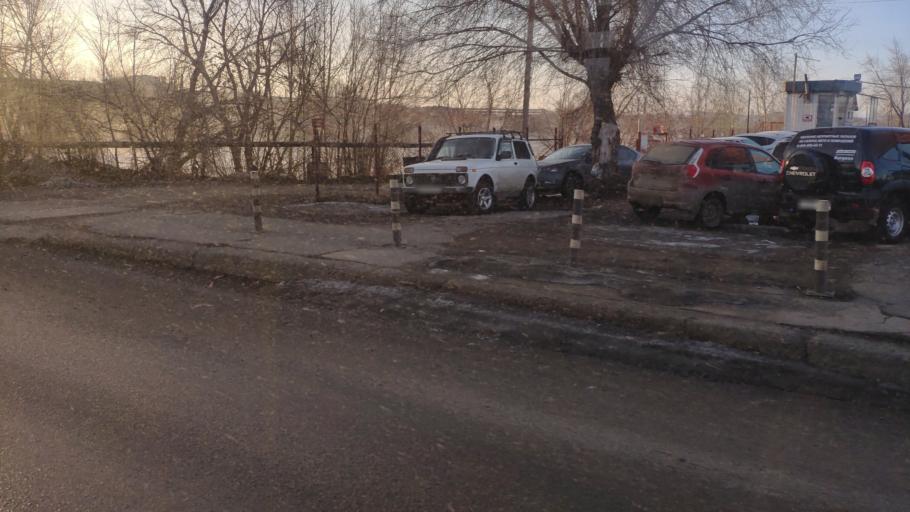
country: RU
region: Chelyabinsk
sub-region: Gorod Magnitogorsk
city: Magnitogorsk
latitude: 53.4222
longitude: 59.0307
